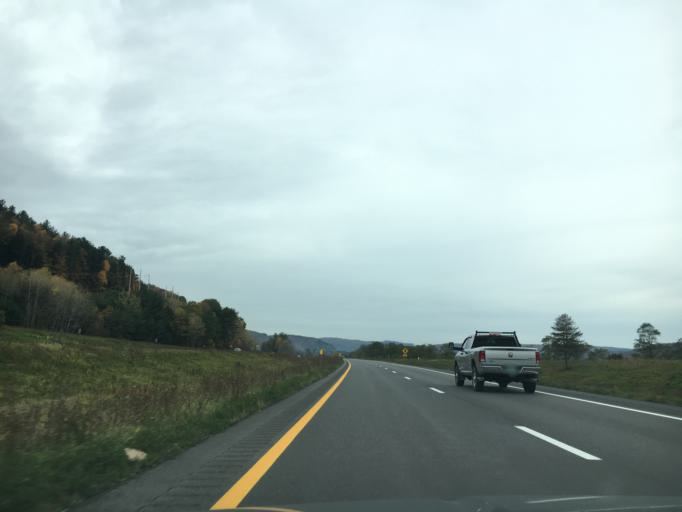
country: US
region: New York
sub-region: Delaware County
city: Sidney
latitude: 42.2938
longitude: -75.4070
